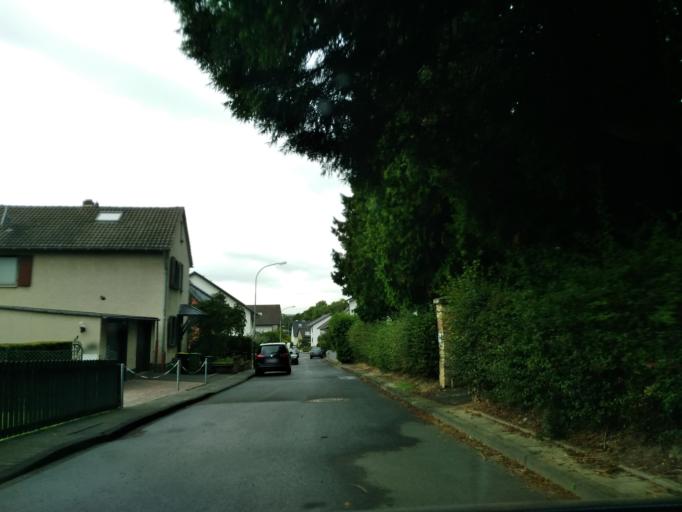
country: DE
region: North Rhine-Westphalia
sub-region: Regierungsbezirk Koln
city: Bad Honnef
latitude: 50.6398
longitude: 7.2444
